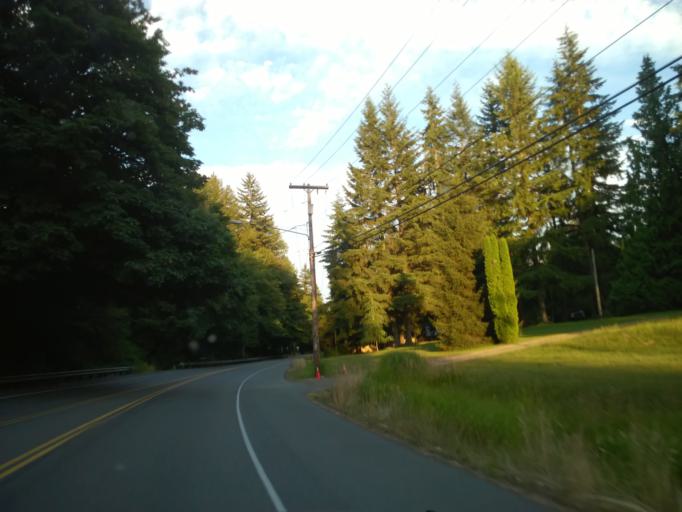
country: US
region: Washington
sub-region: King County
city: Cottage Lake
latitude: 47.7608
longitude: -122.0359
